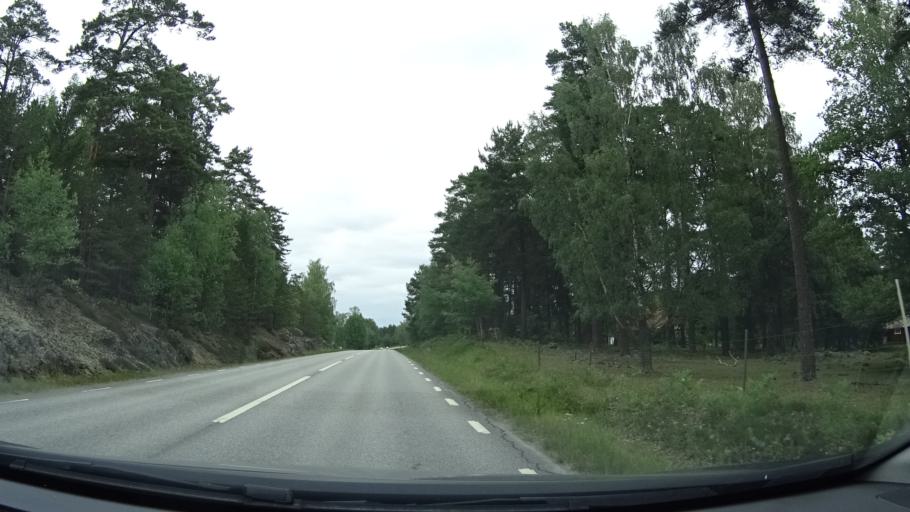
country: SE
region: Stockholm
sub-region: Varmdo Kommun
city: Hemmesta
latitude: 59.3524
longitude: 18.4809
